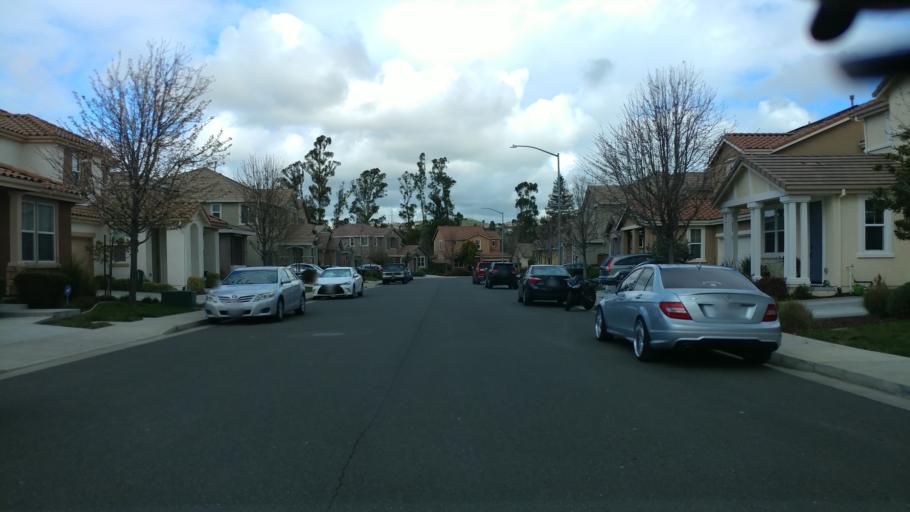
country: US
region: California
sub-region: Contra Costa County
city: Crockett
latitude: 38.0943
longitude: -122.1955
